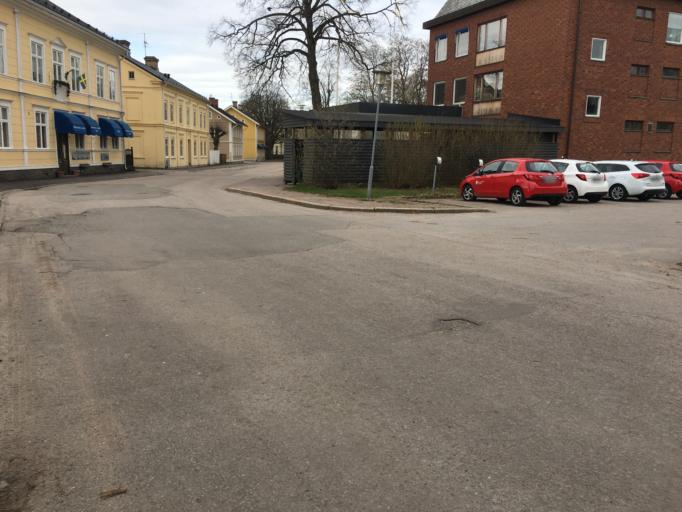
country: SE
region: Vaermland
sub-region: Kristinehamns Kommun
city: Kristinehamn
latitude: 59.3136
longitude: 14.1094
